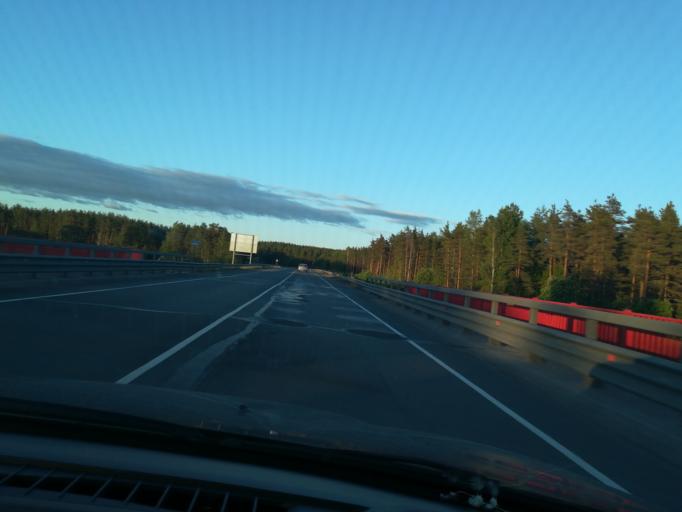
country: RU
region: Leningrad
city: Yakovlevo
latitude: 60.3602
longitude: 29.5350
